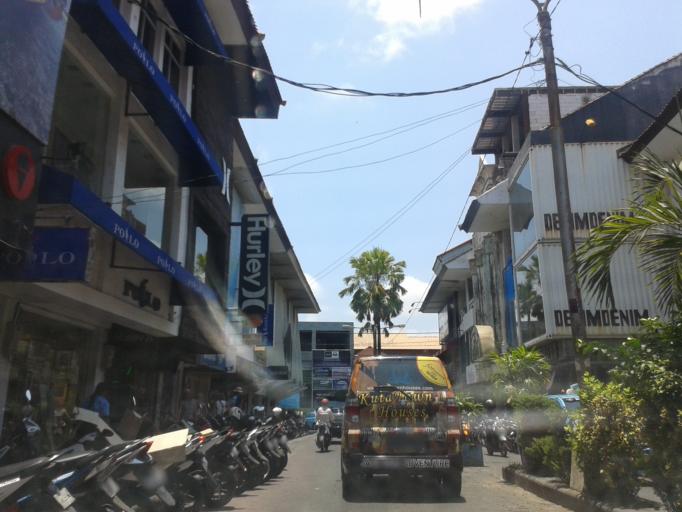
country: ID
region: Bali
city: Kuta
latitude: -8.7232
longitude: 115.1714
